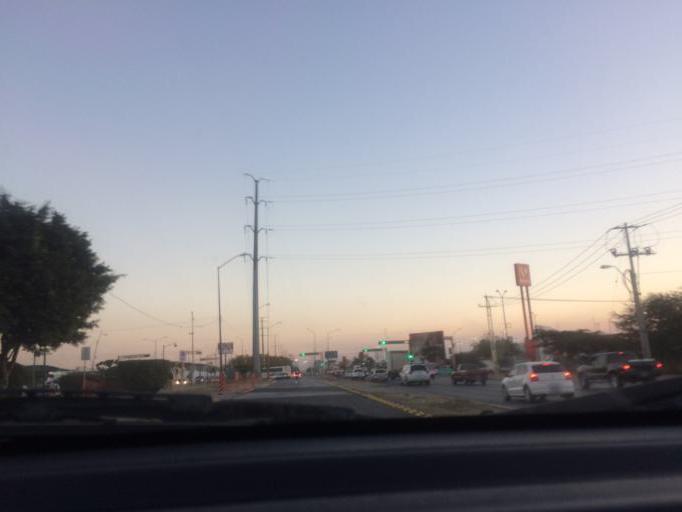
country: MX
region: Guanajuato
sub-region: Leon
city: Medina
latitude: 21.1426
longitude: -101.6331
